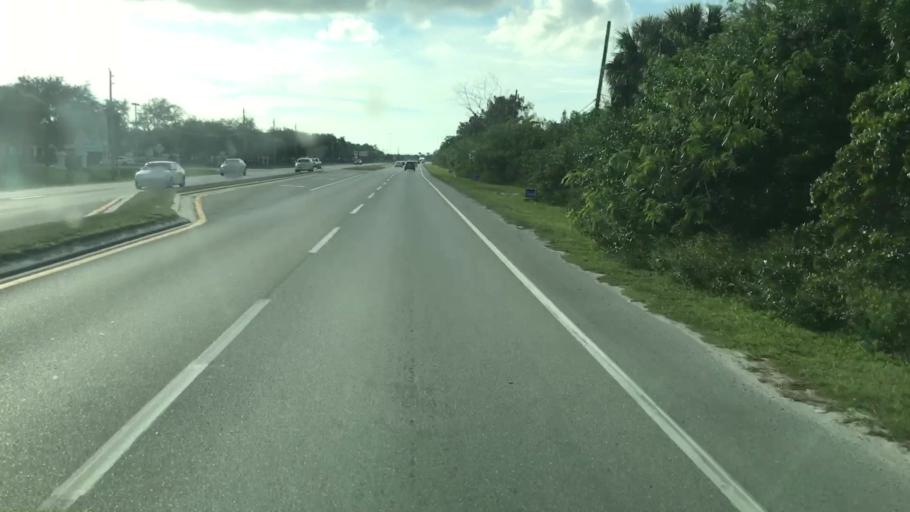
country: US
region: Florida
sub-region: Lee County
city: Bonita Springs
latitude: 26.3316
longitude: -81.7392
